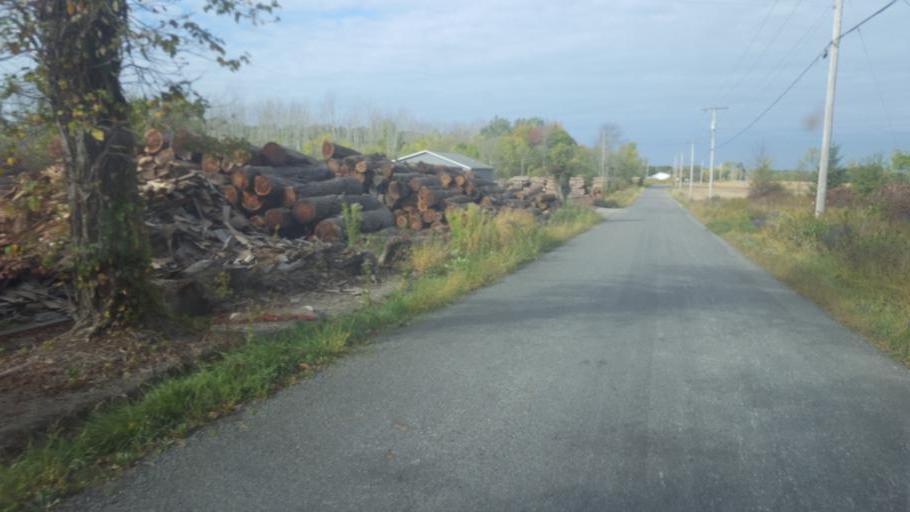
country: US
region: Pennsylvania
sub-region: Mercer County
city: Reynolds Heights
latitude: 41.3297
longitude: -80.3000
